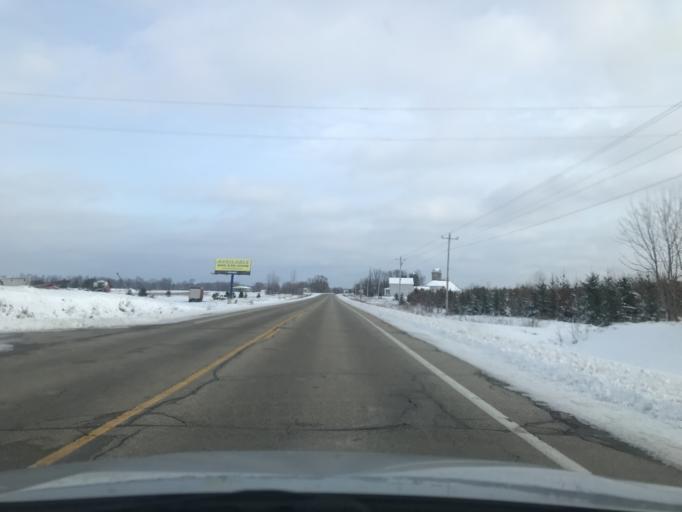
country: US
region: Wisconsin
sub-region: Oconto County
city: Oconto
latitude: 44.8927
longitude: -87.9433
